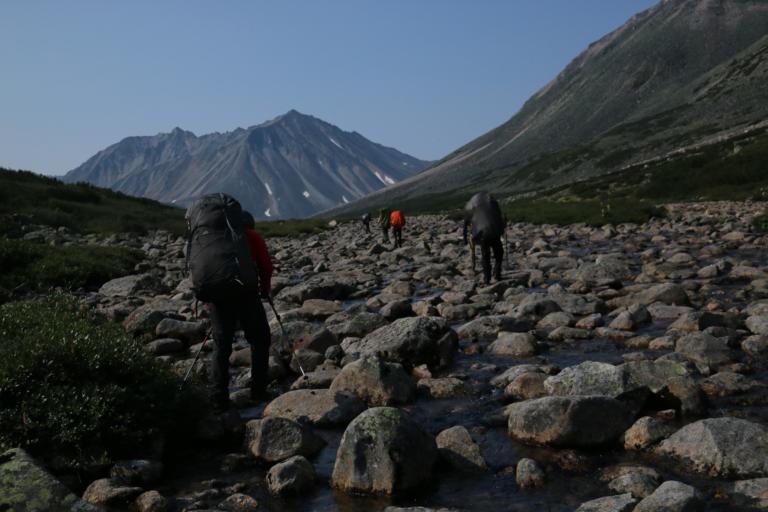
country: RU
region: Respublika Buryatiya
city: Novyy Uoyan
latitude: 56.2403
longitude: 111.0752
